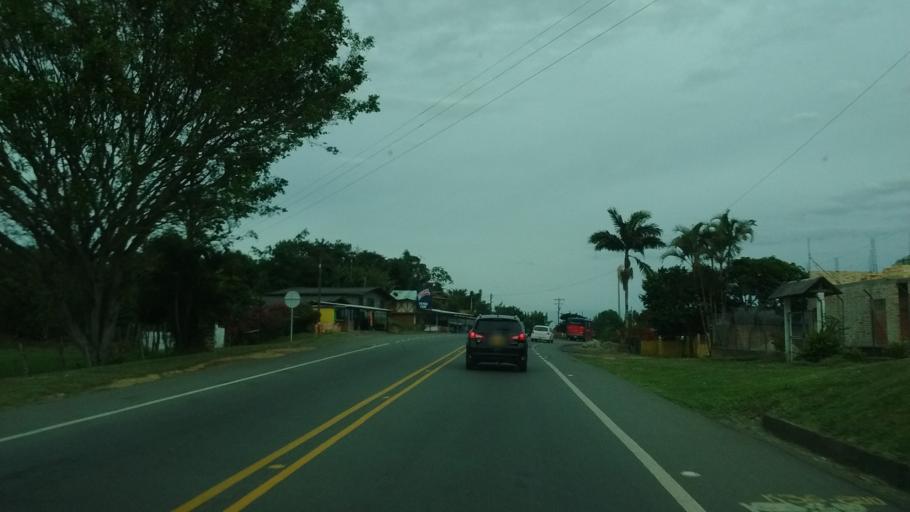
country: CO
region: Cauca
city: Morales
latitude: 2.7379
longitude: -76.5465
